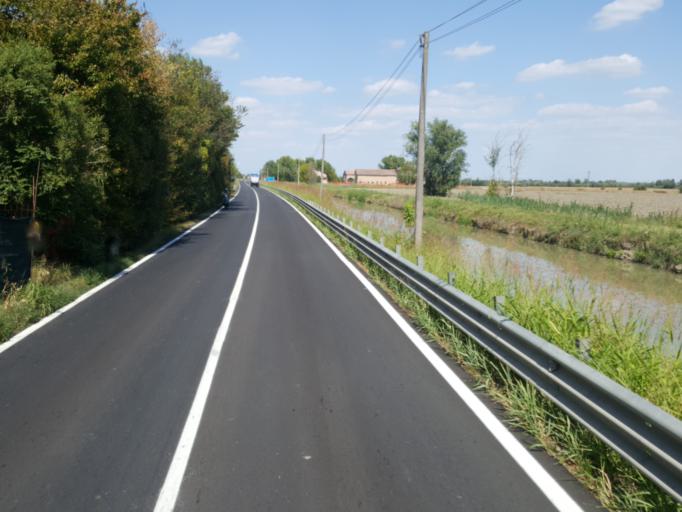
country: IT
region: Emilia-Romagna
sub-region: Provincia di Reggio Emilia
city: Fabbrico
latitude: 44.8865
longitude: 10.7756
